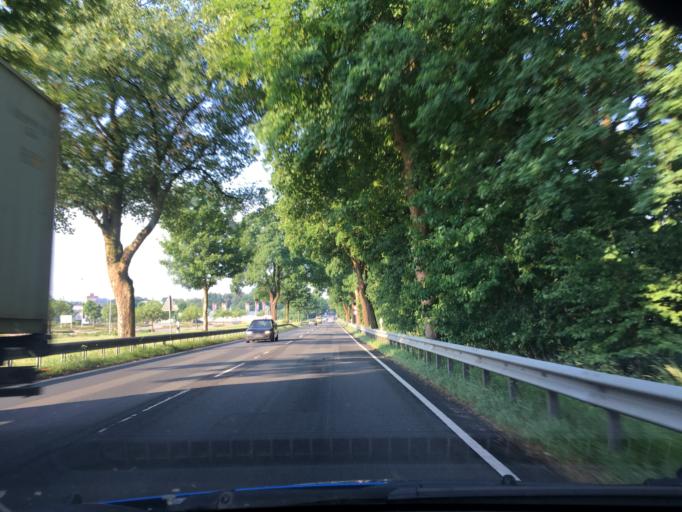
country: DE
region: Lower Saxony
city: Buchholz in der Nordheide
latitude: 53.3523
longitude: 9.8597
